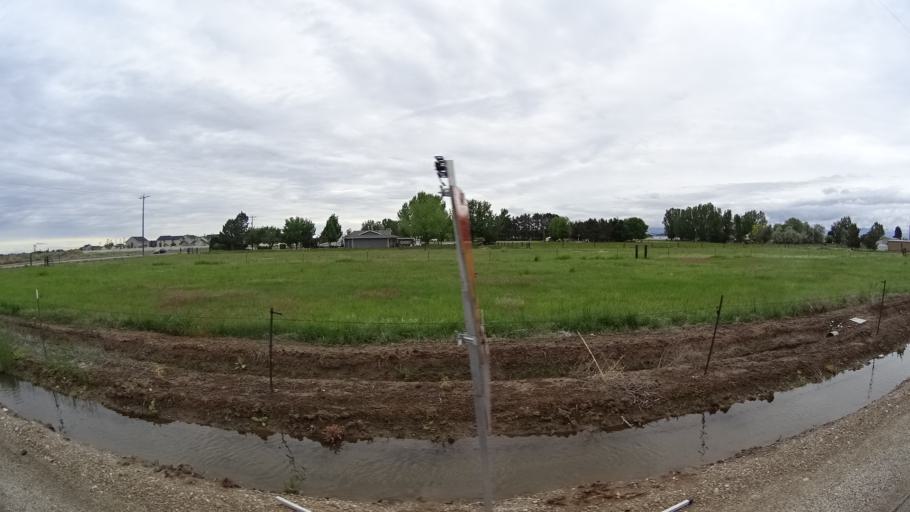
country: US
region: Idaho
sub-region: Ada County
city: Star
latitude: 43.6485
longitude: -116.4525
